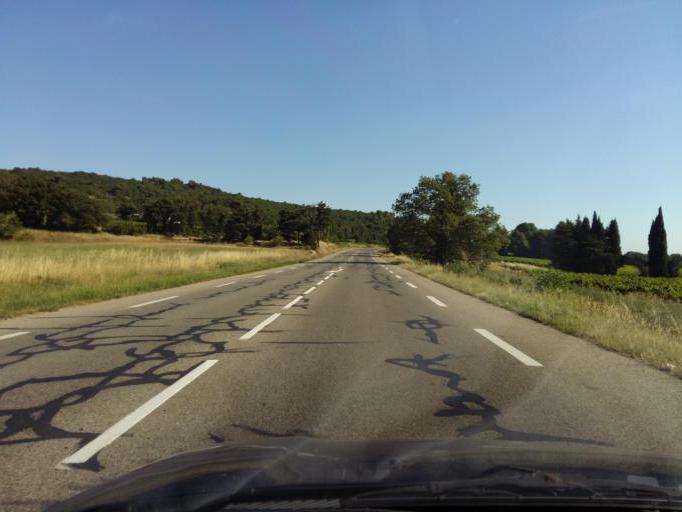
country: FR
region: Provence-Alpes-Cote d'Azur
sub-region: Departement du Vaucluse
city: Visan
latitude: 44.3345
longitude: 4.9472
